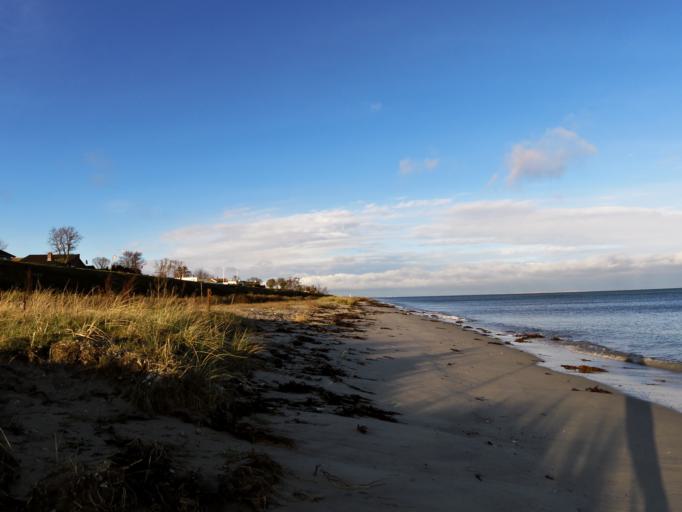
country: DK
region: Central Jutland
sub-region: Arhus Kommune
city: Beder
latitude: 56.0339
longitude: 10.2694
